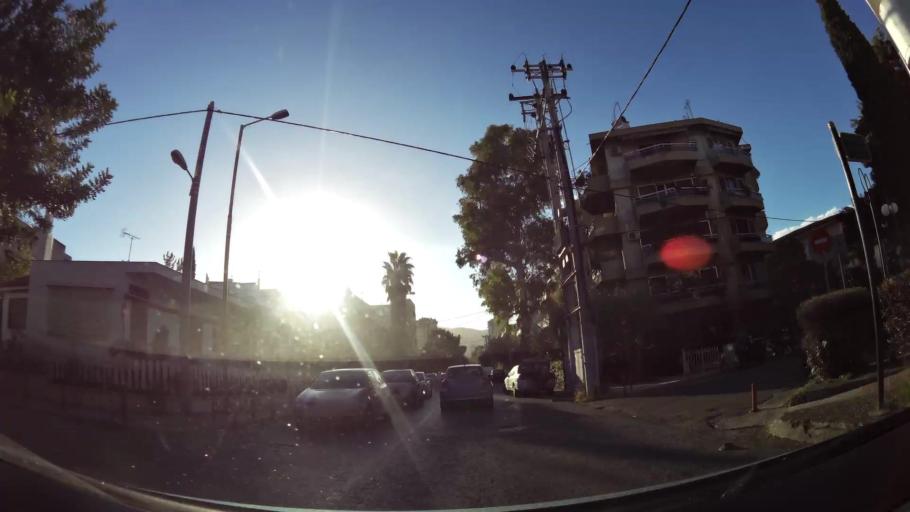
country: GR
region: Attica
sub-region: Nomarchia Athinas
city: Neo Psychiko
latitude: 38.0068
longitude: 23.7881
